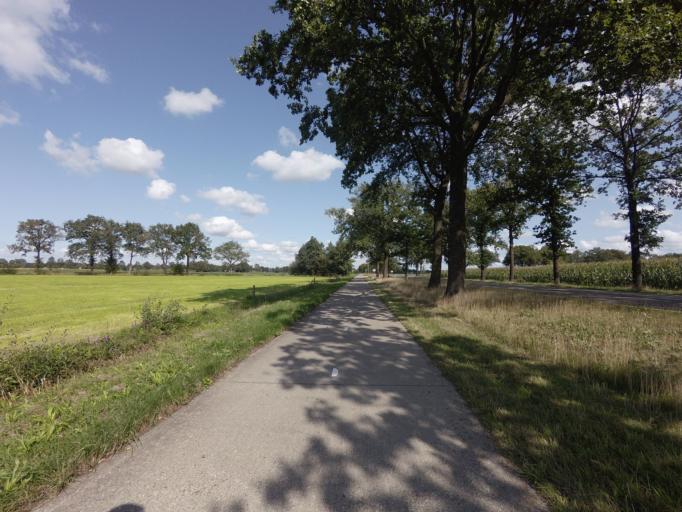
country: NL
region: Overijssel
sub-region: Gemeente Dalfsen
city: Dalfsen
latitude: 52.5557
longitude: 6.2618
